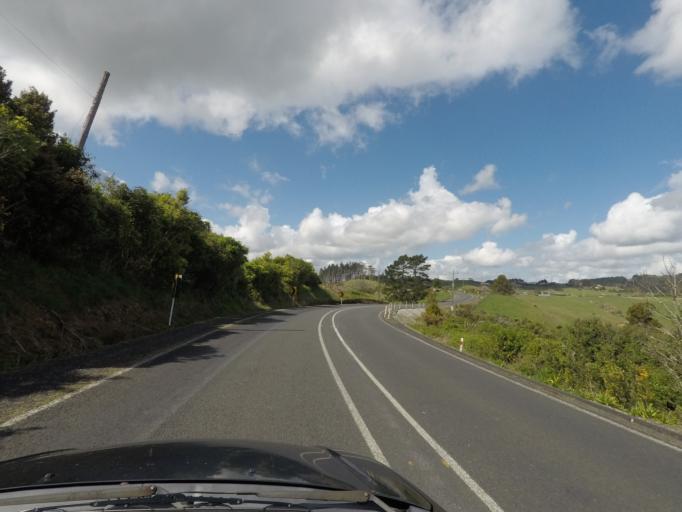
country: NZ
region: Auckland
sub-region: Auckland
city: Pukekohe East
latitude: -37.1434
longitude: 175.0097
